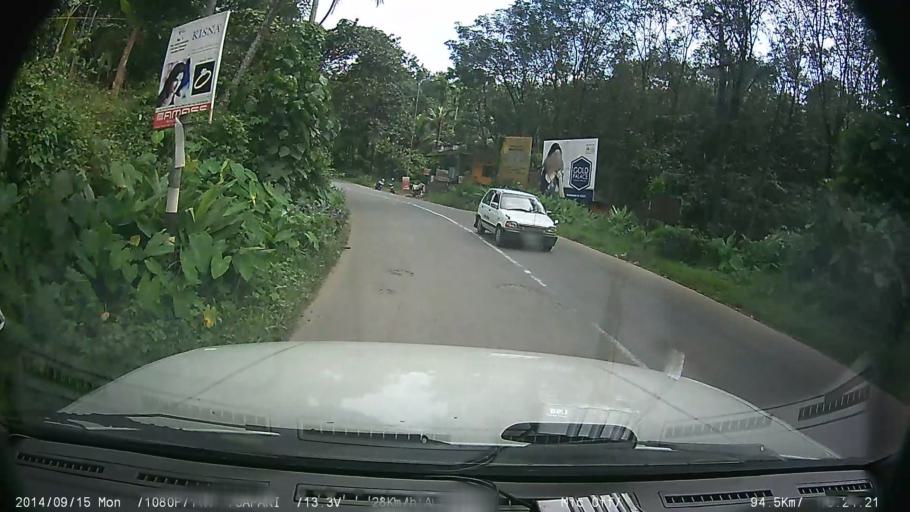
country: IN
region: Kerala
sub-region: Ernakulam
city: Muvattupuzha
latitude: 9.8912
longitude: 76.5892
